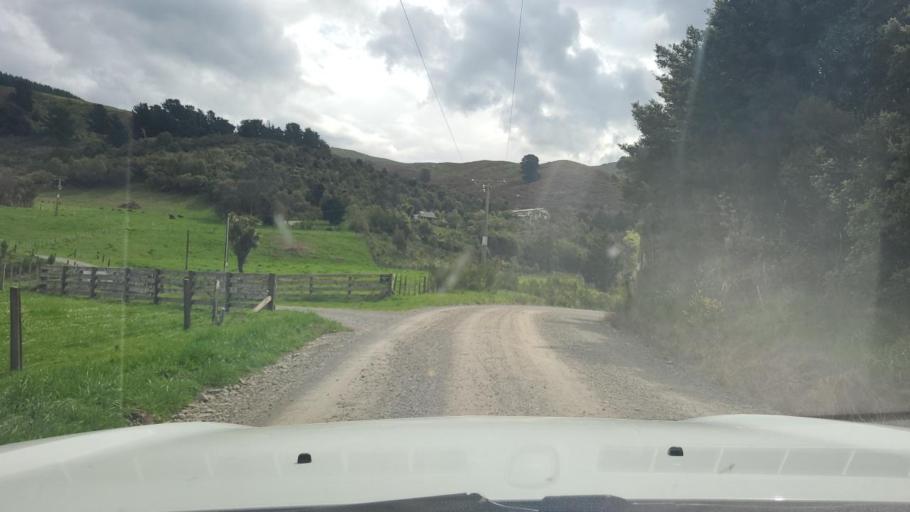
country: NZ
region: Wellington
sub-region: Masterton District
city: Masterton
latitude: -40.9933
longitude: 175.4828
